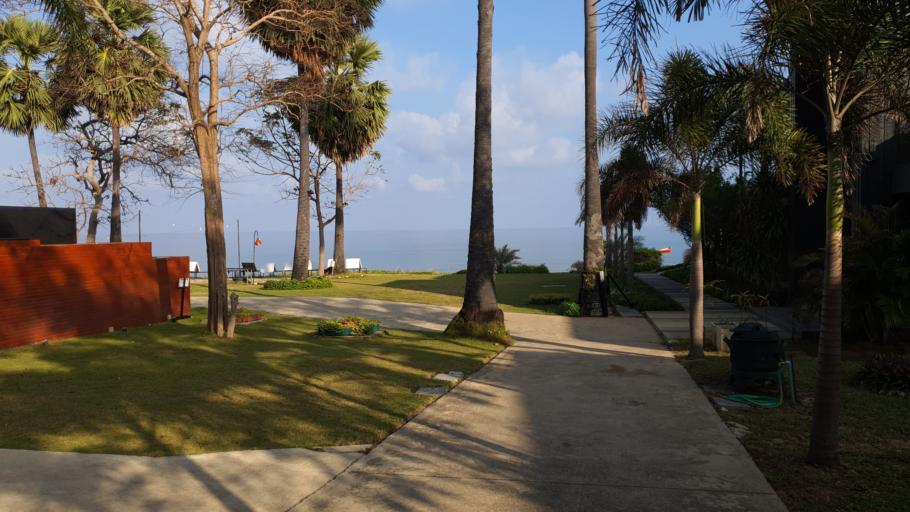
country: TH
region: Prachuap Khiri Khan
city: Thap Sakae
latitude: 11.4105
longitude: 99.5981
